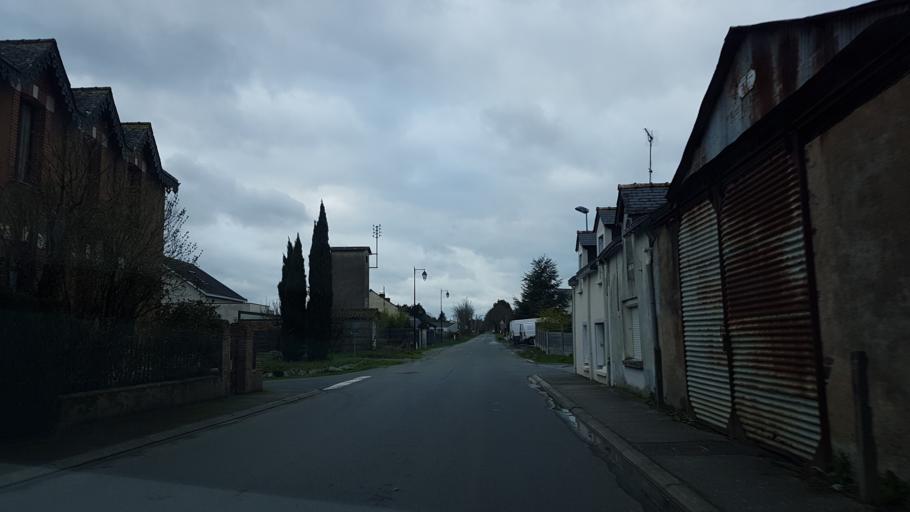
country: FR
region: Pays de la Loire
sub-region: Departement de la Loire-Atlantique
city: Le Gavre
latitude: 47.5220
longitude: -1.7515
